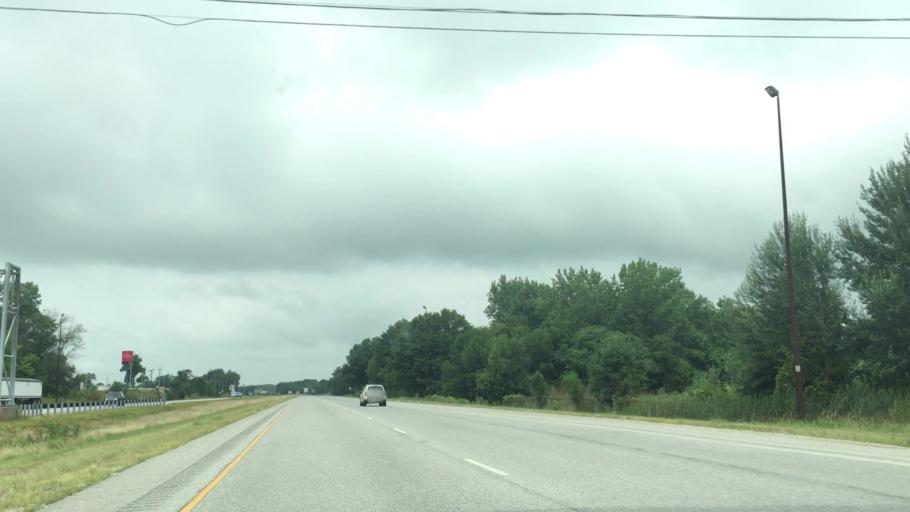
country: US
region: Illinois
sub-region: Rock Island County
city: Coal Valley
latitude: 41.4581
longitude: -90.4996
